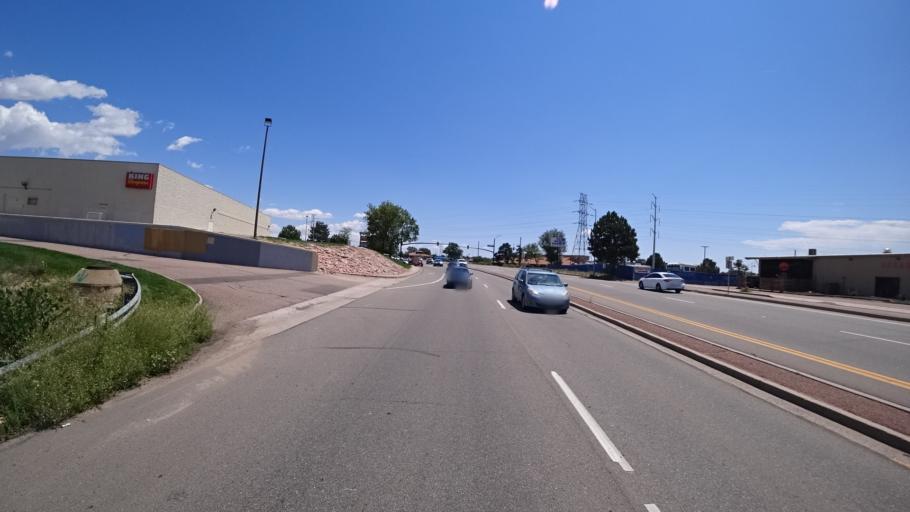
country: US
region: Colorado
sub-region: El Paso County
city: Stratmoor
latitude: 38.7900
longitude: -104.7617
